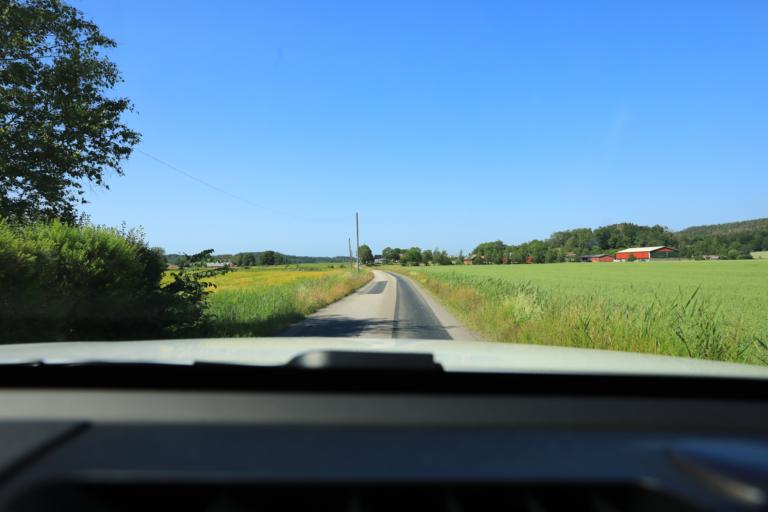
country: SE
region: Halland
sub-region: Varbergs Kommun
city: Veddige
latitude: 57.2019
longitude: 12.3192
